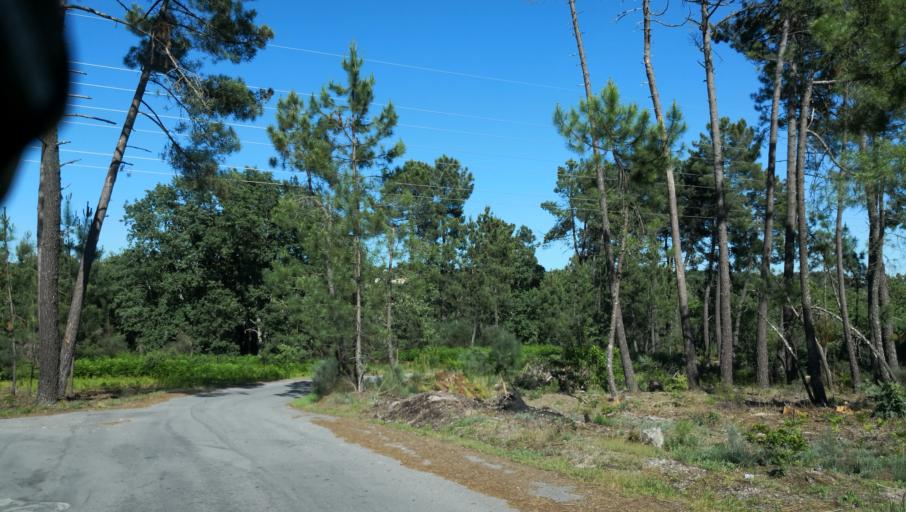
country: PT
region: Vila Real
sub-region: Vila Real
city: Vila Real
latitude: 41.2997
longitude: -7.6697
